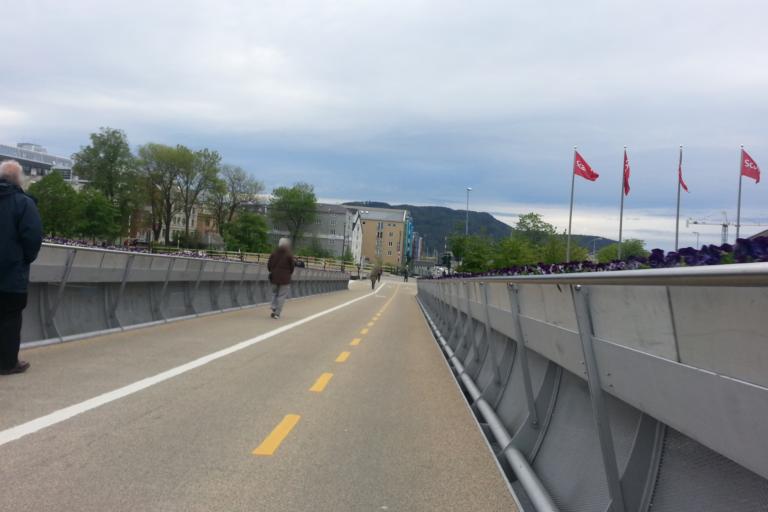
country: NO
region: Sor-Trondelag
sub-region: Trondheim
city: Trondheim
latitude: 63.4353
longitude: 10.4071
